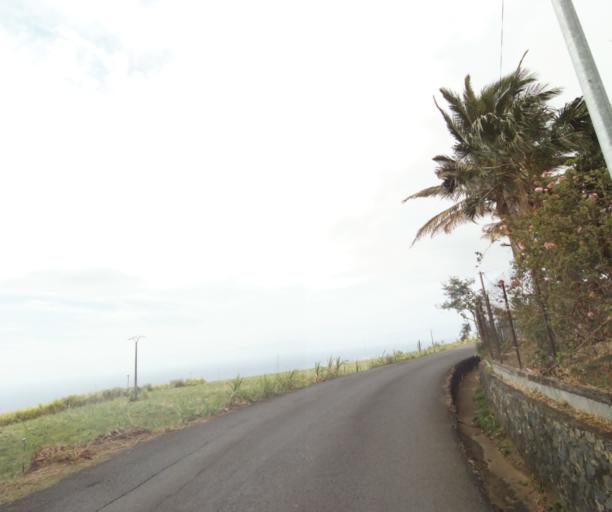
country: RE
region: Reunion
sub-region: Reunion
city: Saint-Paul
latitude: -21.0346
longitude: 55.2899
